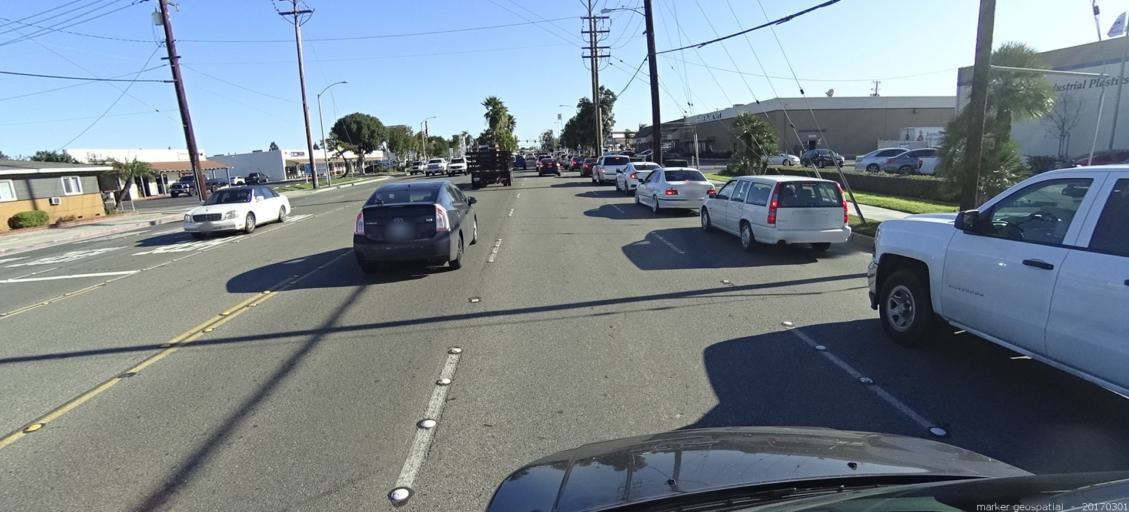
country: US
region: California
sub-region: Orange County
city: Placentia
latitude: 33.8532
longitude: -117.8581
